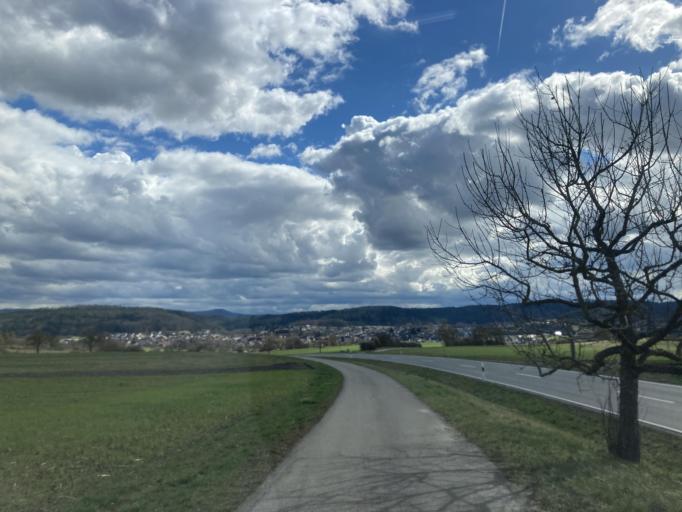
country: DE
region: Baden-Wuerttemberg
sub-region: Tuebingen Region
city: Rangendingen
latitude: 48.3950
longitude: 8.8824
